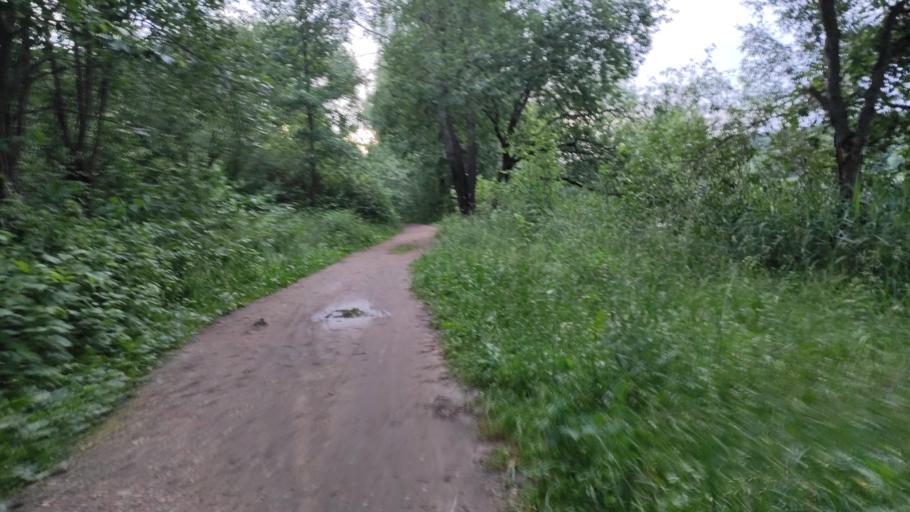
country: BY
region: Minsk
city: Zhdanovichy
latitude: 53.9633
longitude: 27.4413
